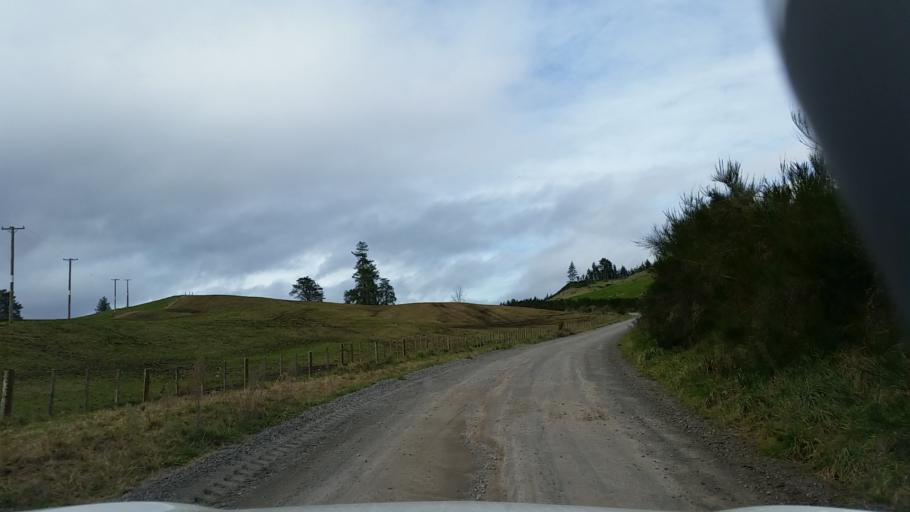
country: NZ
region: Bay of Plenty
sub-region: Whakatane District
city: Murupara
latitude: -38.3382
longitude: 176.5393
